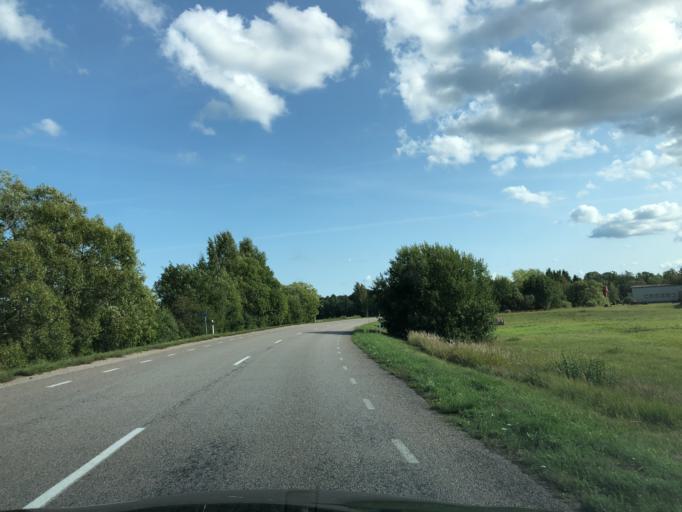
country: EE
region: Hiiumaa
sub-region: Kaerdla linn
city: Kardla
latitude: 58.7117
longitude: 22.5851
